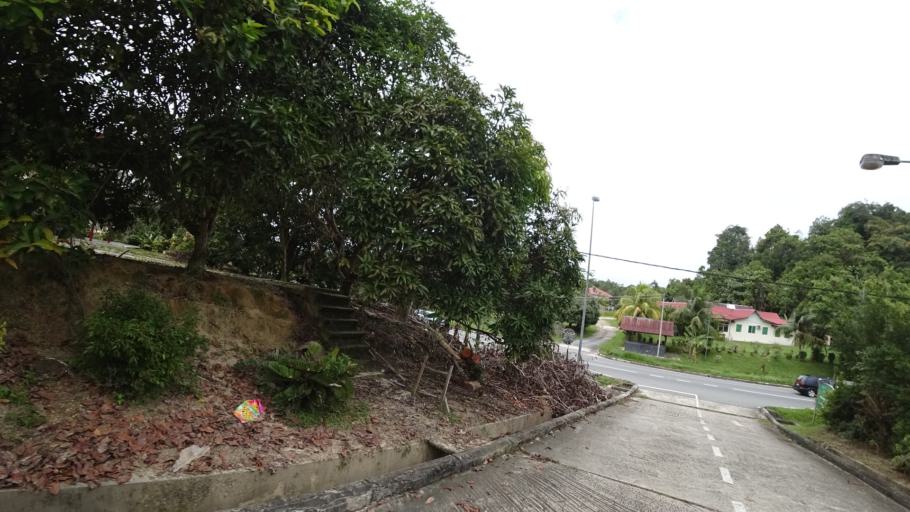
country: BN
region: Tutong
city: Tutong
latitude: 4.8056
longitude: 114.7645
